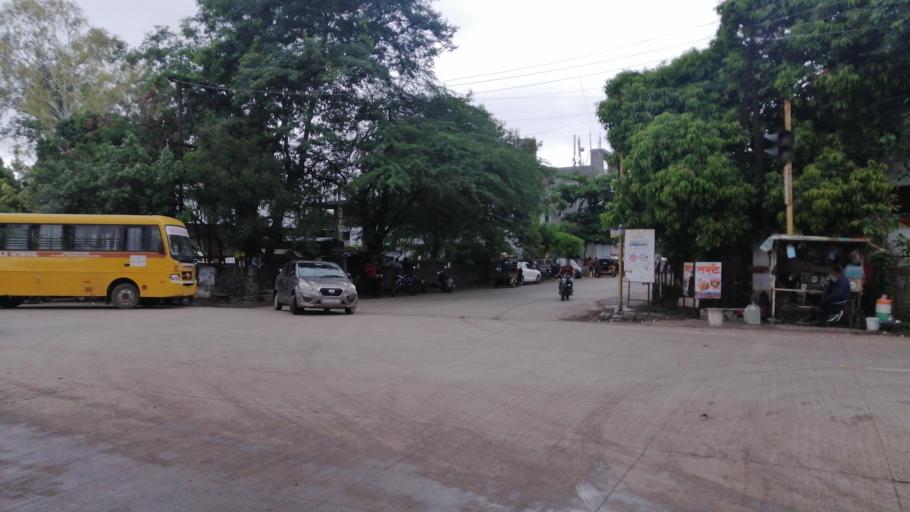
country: IN
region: Maharashtra
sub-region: Aurangabad Division
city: Aurangabad
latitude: 19.8785
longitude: 75.3713
